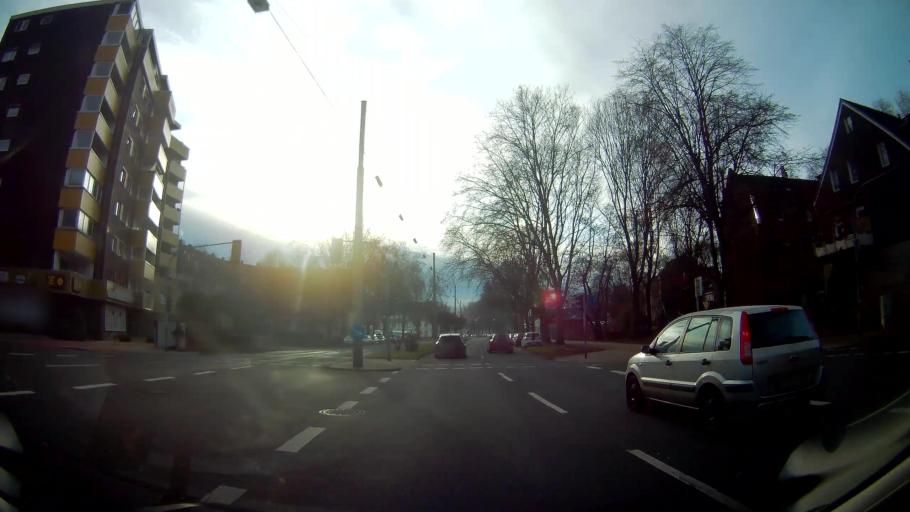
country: DE
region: North Rhine-Westphalia
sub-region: Regierungsbezirk Arnsberg
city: Herne
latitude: 51.5406
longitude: 7.2177
